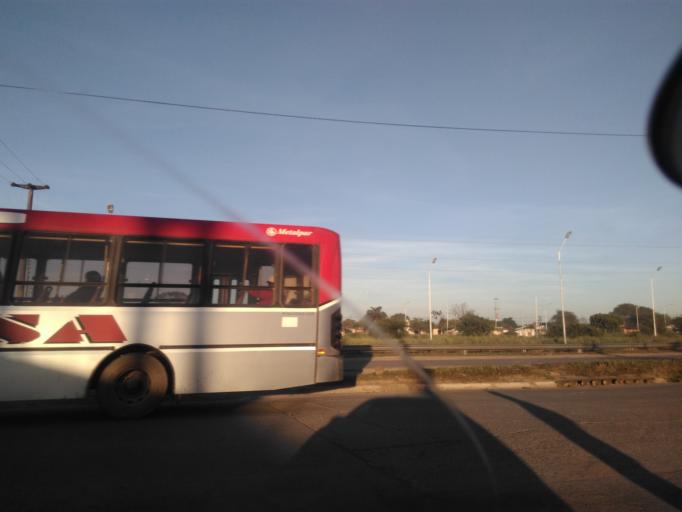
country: AR
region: Chaco
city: Resistencia
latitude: -27.4726
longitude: -59.0052
